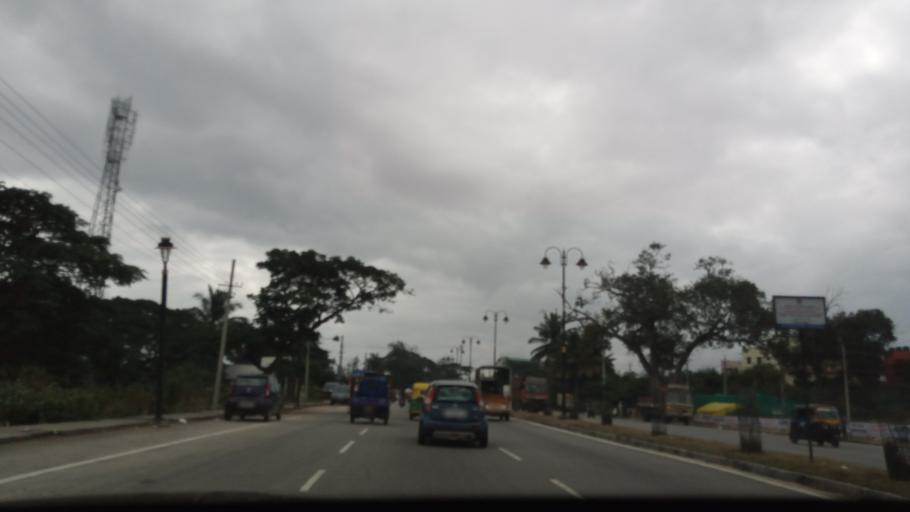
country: IN
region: Karnataka
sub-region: Mysore
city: Mysore
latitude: 12.3493
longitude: 76.6607
